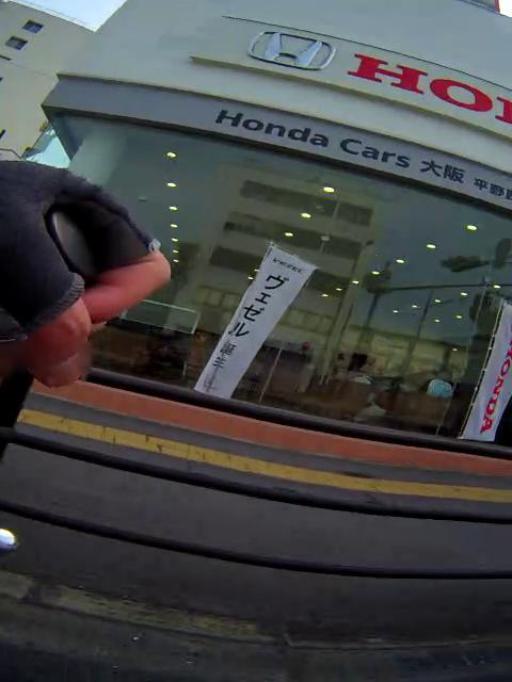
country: JP
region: Osaka
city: Yao
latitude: 34.6321
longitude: 135.5453
